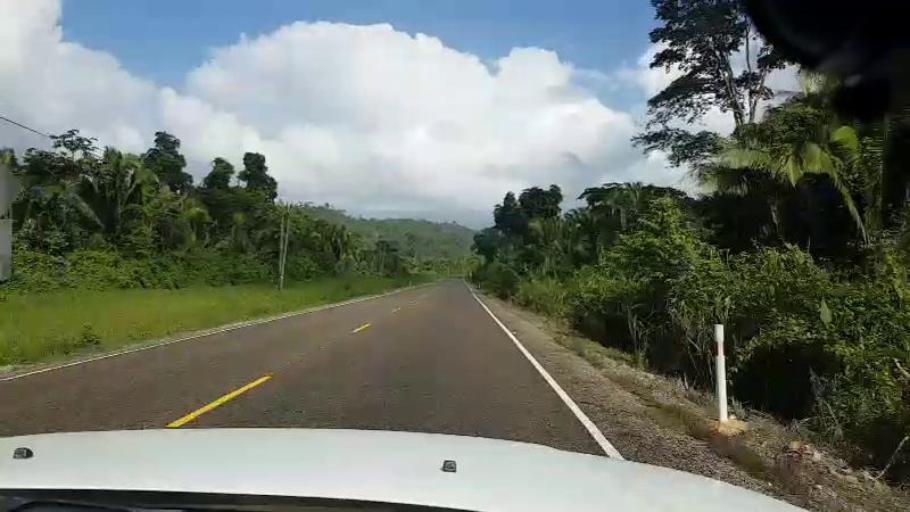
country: BZ
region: Cayo
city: Belmopan
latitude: 17.1464
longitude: -88.7278
